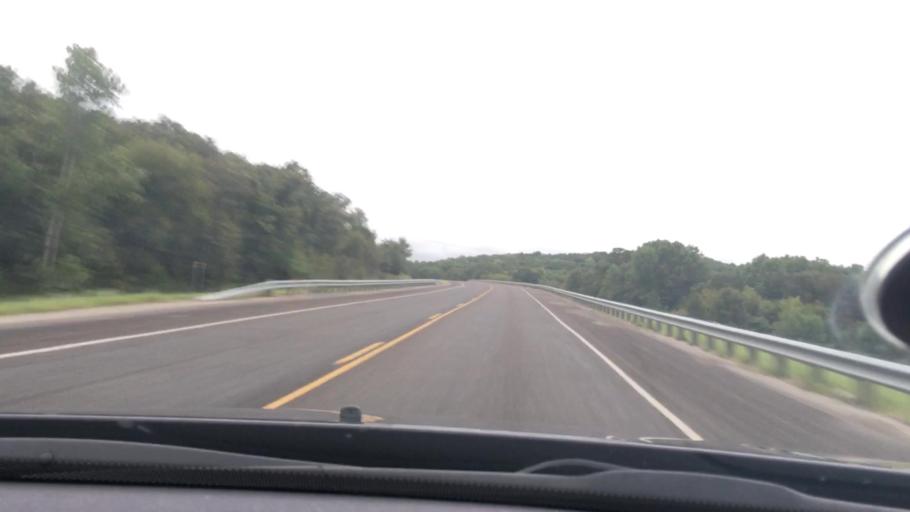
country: US
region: Oklahoma
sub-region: Sequoyah County
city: Vian
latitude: 35.5300
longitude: -94.9734
